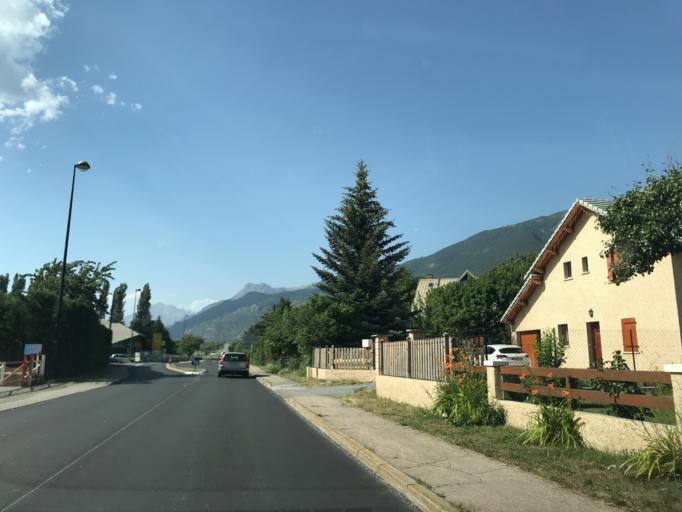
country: FR
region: Provence-Alpes-Cote d'Azur
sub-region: Departement des Hautes-Alpes
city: Guillestre
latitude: 44.6751
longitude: 6.6171
